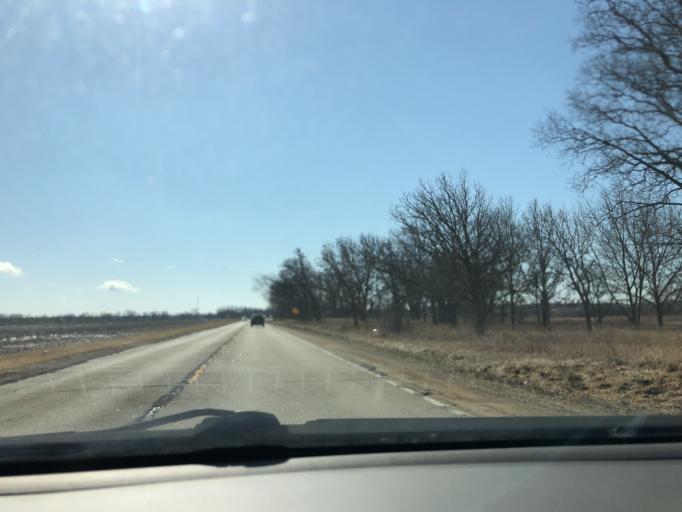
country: US
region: Illinois
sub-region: Kane County
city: Pingree Grove
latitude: 42.0990
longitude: -88.4546
